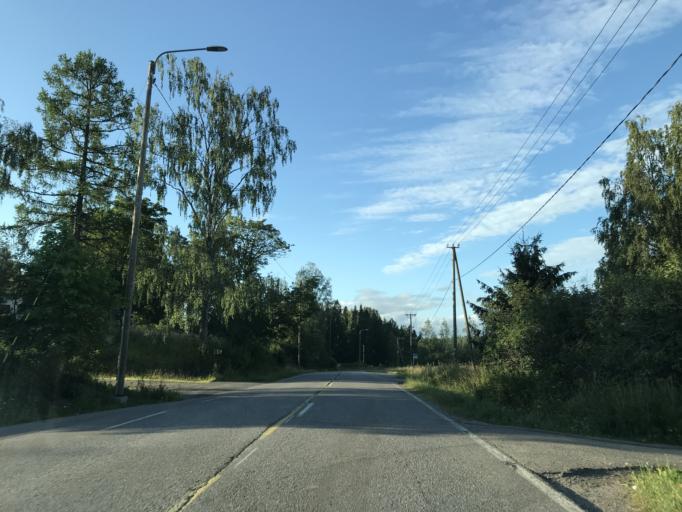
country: FI
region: Uusimaa
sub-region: Helsinki
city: Nurmijaervi
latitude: 60.3678
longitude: 24.6820
